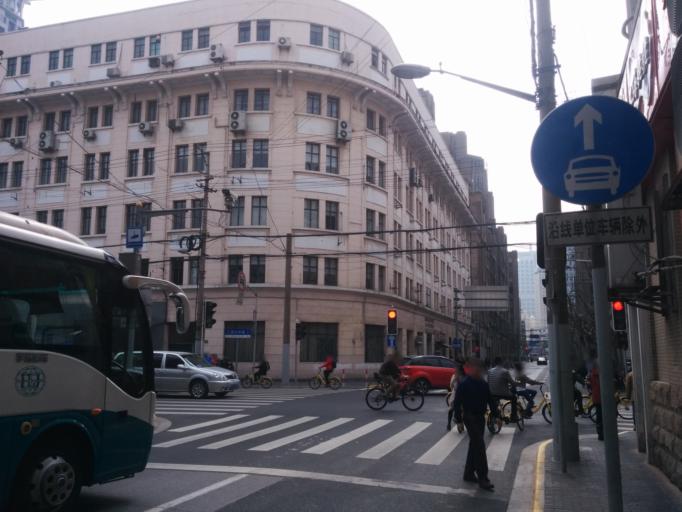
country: CN
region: Shanghai Shi
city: Hongkou
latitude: 31.2373
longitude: 121.4848
